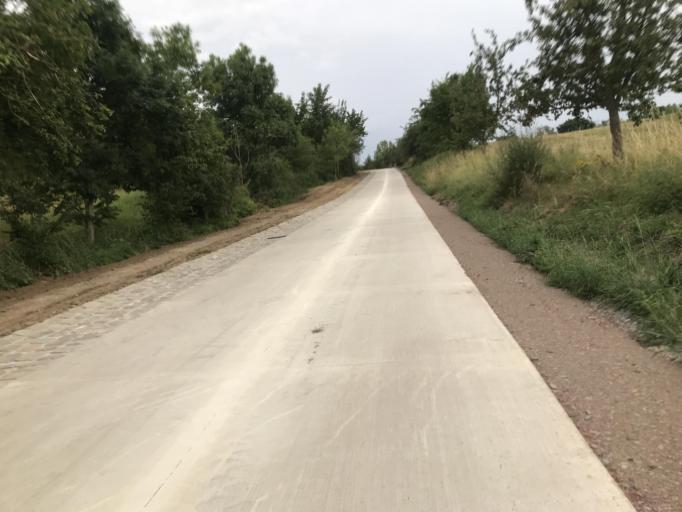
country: DE
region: Saxony-Anhalt
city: Harsleben
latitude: 51.8602
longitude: 11.0857
